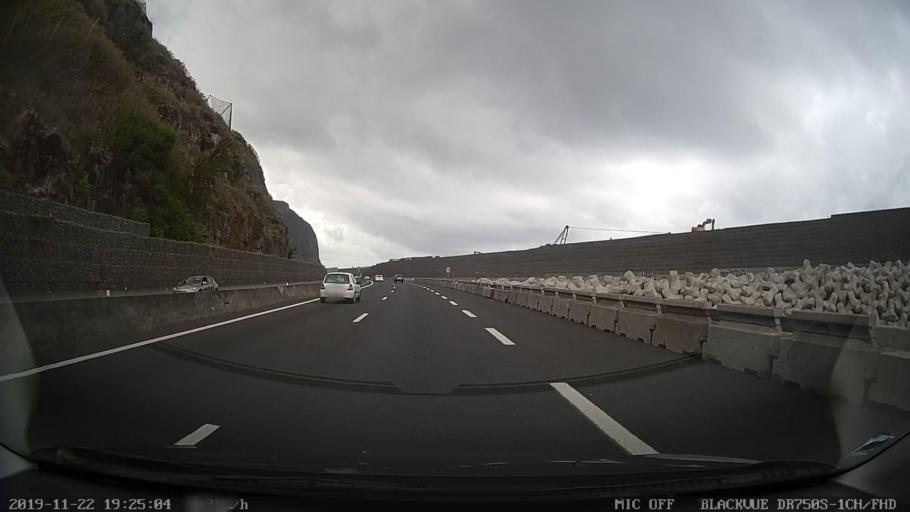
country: RE
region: Reunion
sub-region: Reunion
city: La Possession
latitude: -20.8917
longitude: 55.3818
